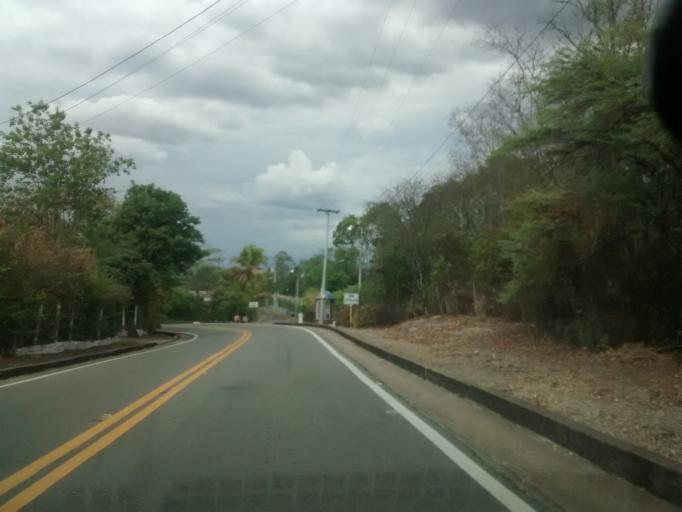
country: CO
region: Cundinamarca
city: Agua de Dios
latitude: 4.4176
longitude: -74.7084
